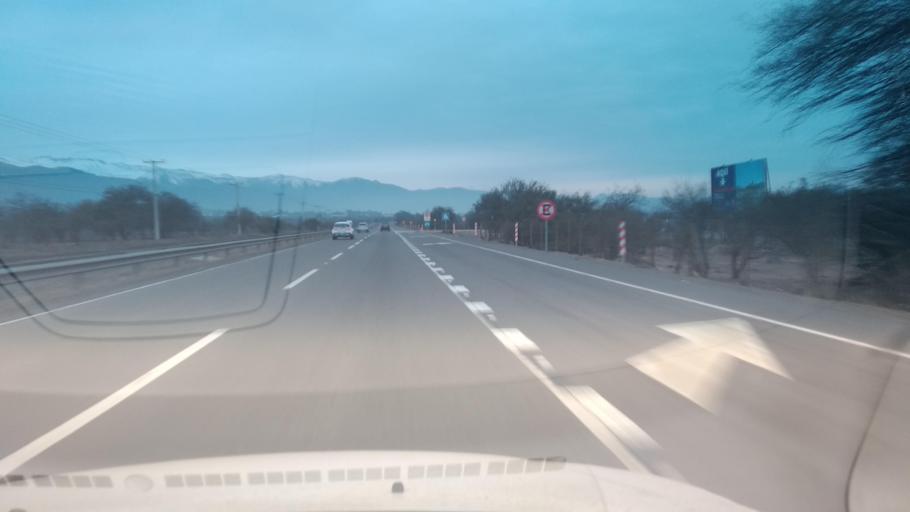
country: CL
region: Santiago Metropolitan
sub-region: Provincia de Chacabuco
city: Chicureo Abajo
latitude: -33.1224
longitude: -70.6773
